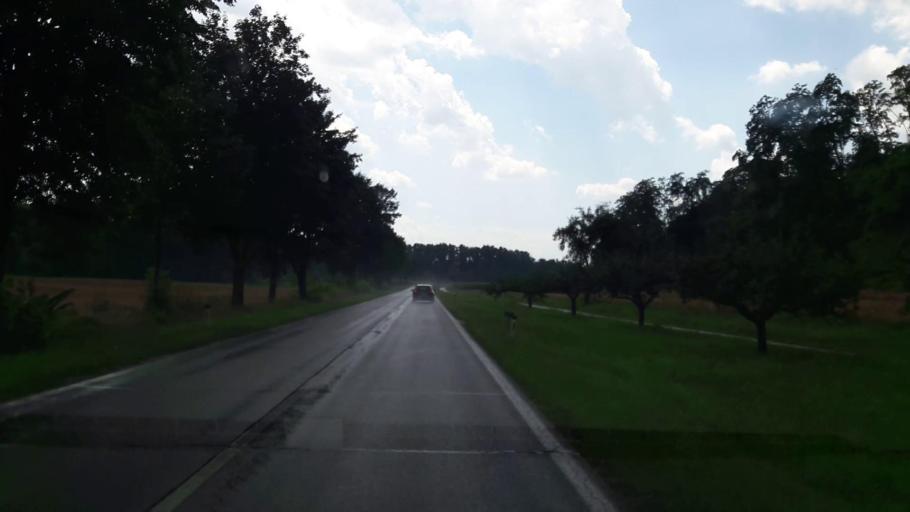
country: AT
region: Lower Austria
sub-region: Politischer Bezirk Melk
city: Emmersdorf an der Donau
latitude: 48.2577
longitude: 15.3600
